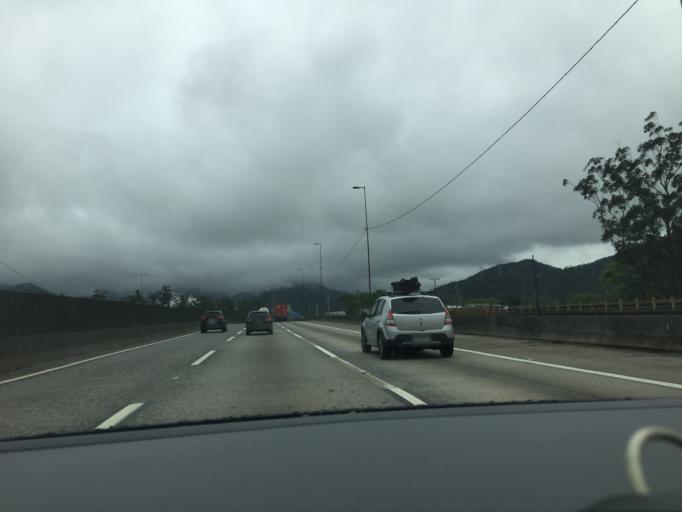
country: BR
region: Sao Paulo
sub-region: Cubatao
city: Cubatao
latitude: -23.8780
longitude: -46.4253
